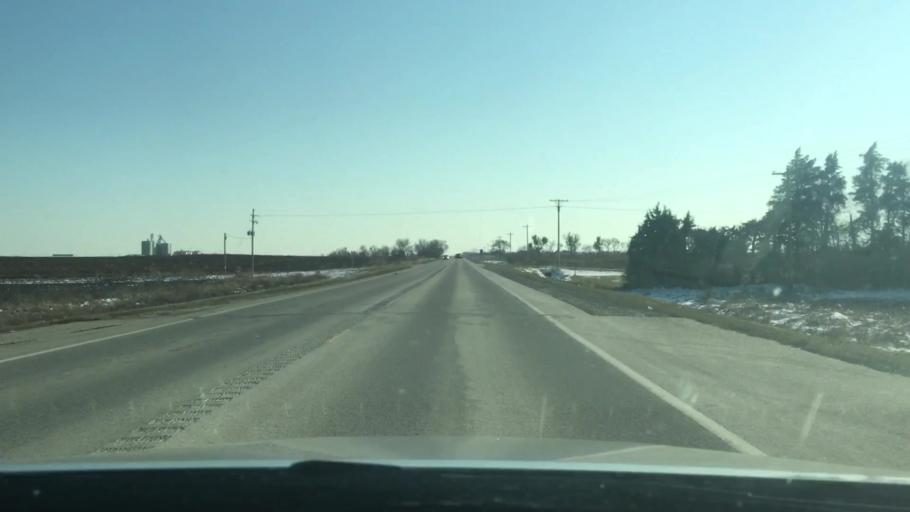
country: US
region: Kansas
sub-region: Rice County
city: Lyons
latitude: 38.3053
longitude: -98.2019
